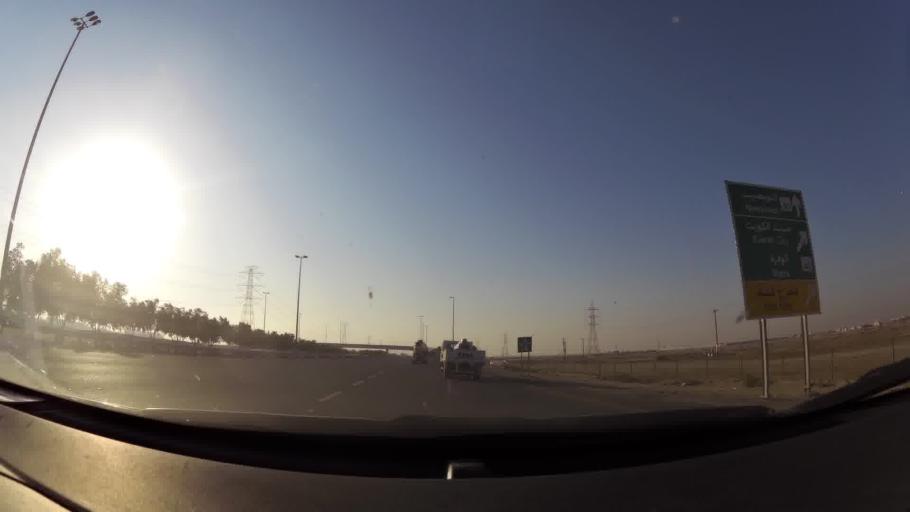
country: SA
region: Eastern Province
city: Al Khafji
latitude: 28.7250
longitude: 48.2873
